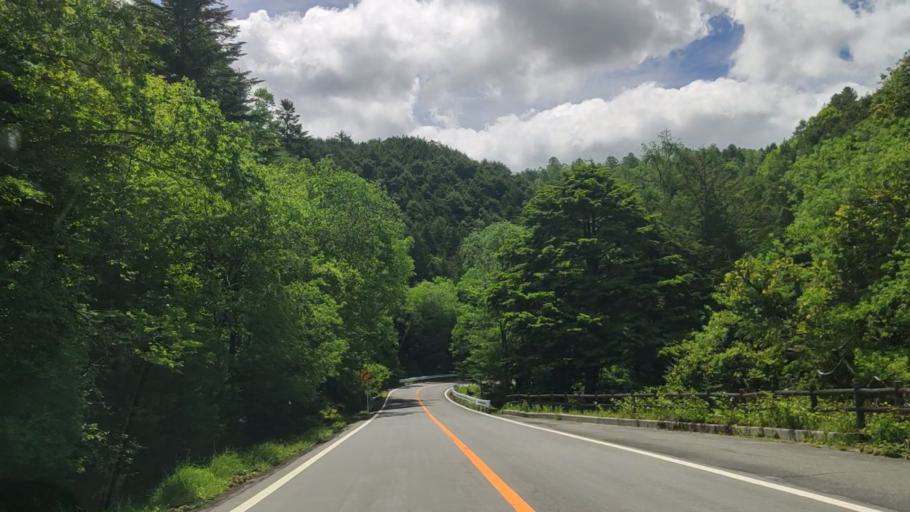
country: JP
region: Nagano
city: Chino
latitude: 36.0800
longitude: 138.2924
